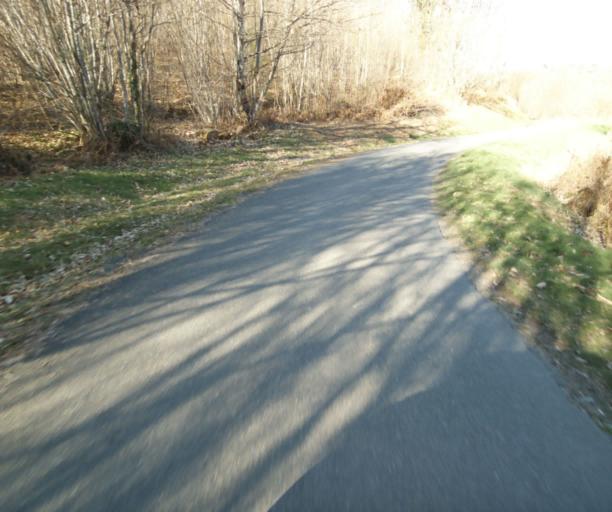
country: FR
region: Limousin
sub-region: Departement de la Correze
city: Chamboulive
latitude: 45.4134
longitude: 1.6500
